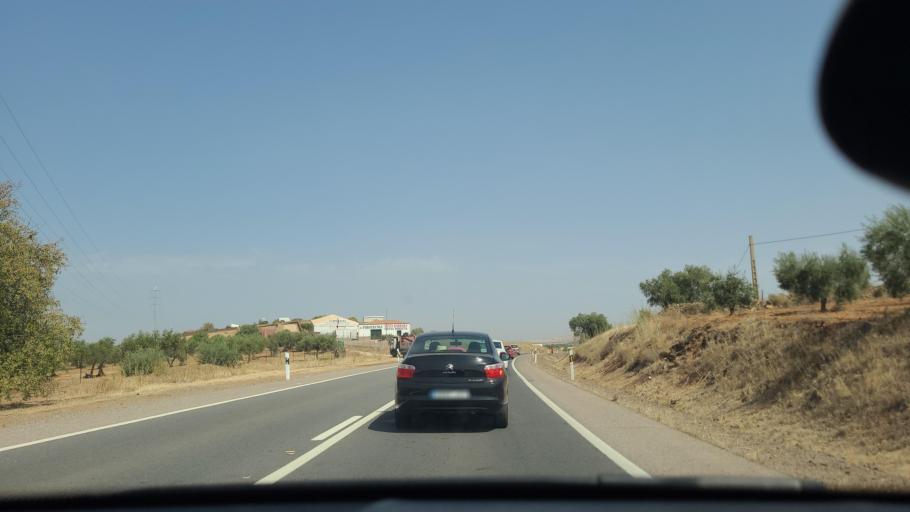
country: ES
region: Extremadura
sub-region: Provincia de Badajoz
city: Zafra
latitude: 38.4429
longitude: -6.4253
